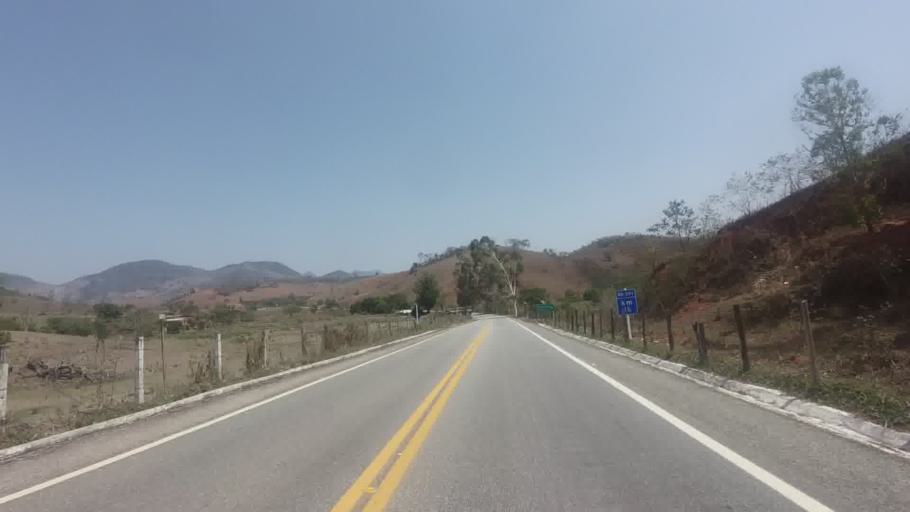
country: BR
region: Espirito Santo
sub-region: Jeronimo Monteiro
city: Jeronimo Monteiro
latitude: -20.8771
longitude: -41.2666
